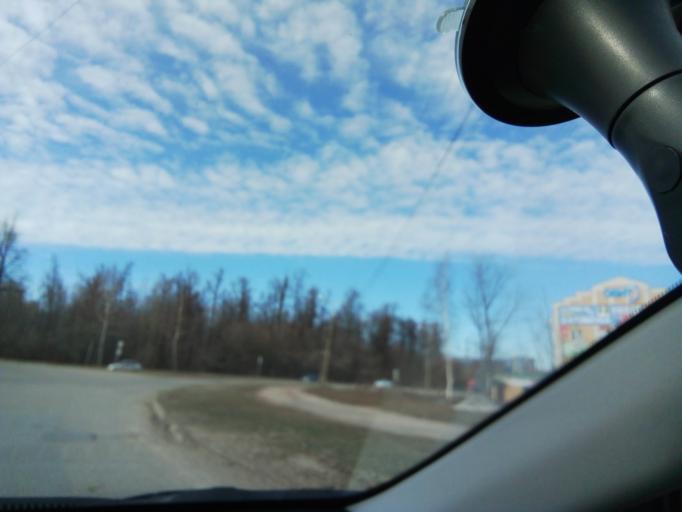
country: RU
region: Chuvashia
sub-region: Cheboksarskiy Rayon
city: Cheboksary
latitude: 56.0968
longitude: 47.2597
